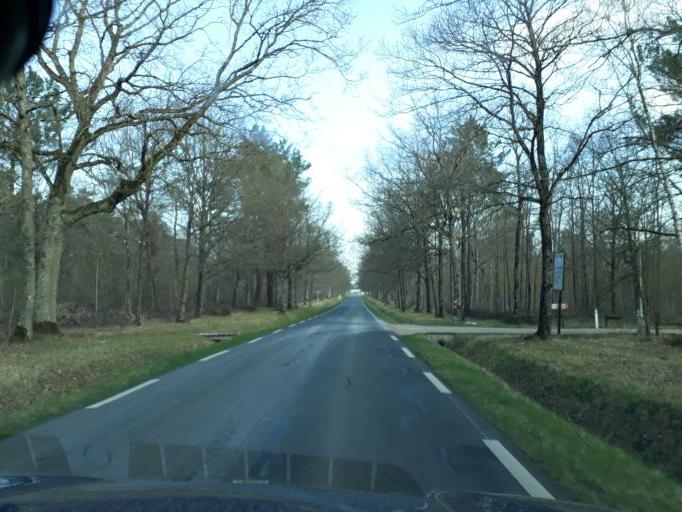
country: FR
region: Centre
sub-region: Departement du Loiret
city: Chaingy
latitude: 47.9288
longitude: 1.7730
